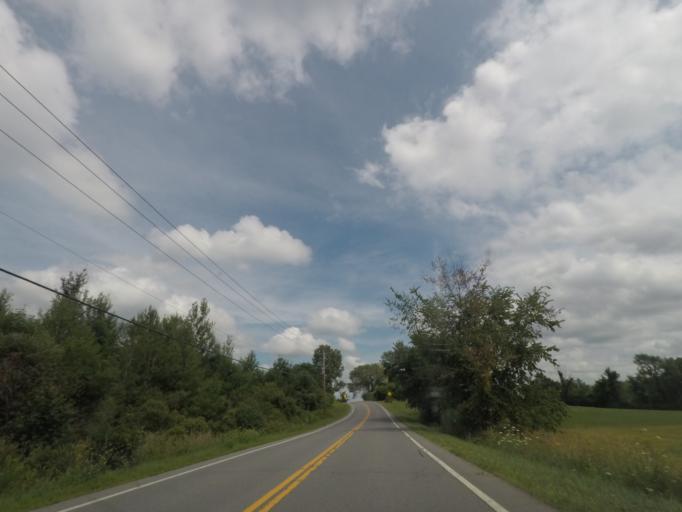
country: US
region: New York
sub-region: Saratoga County
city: Stillwater
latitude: 43.0239
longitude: -73.6732
